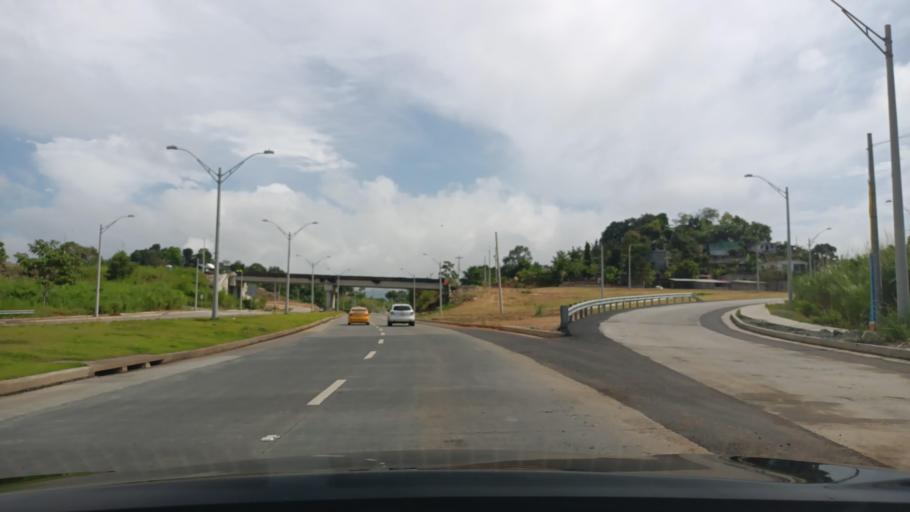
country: PA
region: Panama
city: Las Cumbres
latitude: 9.1007
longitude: -79.4998
